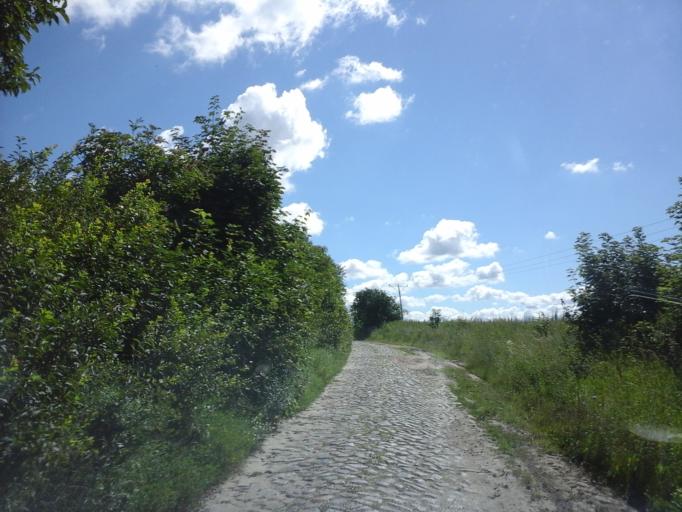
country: PL
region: West Pomeranian Voivodeship
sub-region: Powiat choszczenski
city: Recz
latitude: 53.2123
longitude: 15.5070
